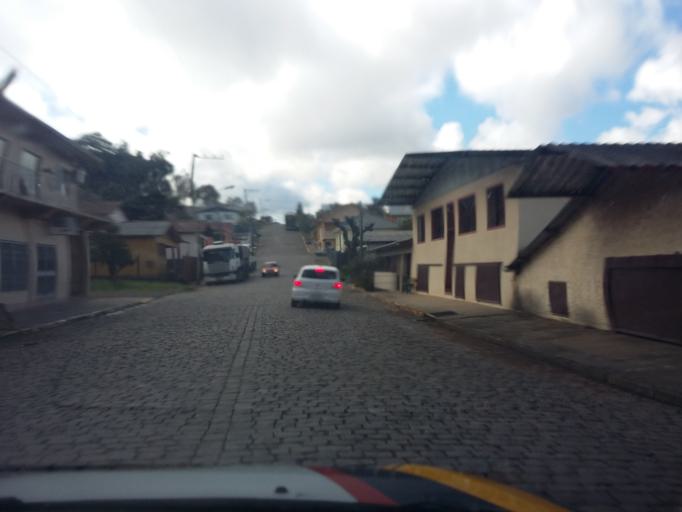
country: BR
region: Rio Grande do Sul
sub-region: Sao Marcos
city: Sao Marcos
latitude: -28.7971
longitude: -51.0948
